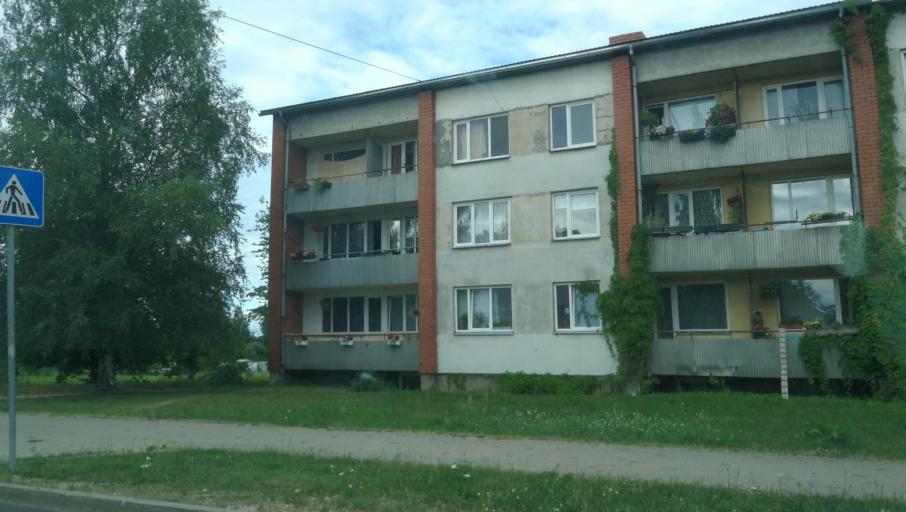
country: LV
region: Cesu Rajons
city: Cesis
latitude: 57.3065
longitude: 25.2952
